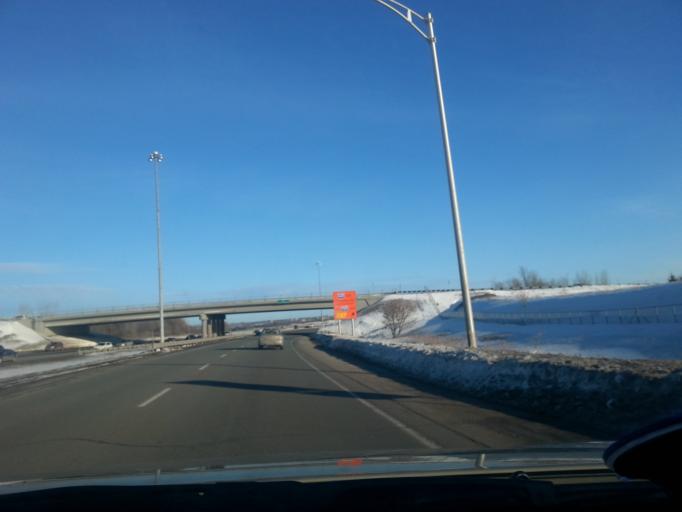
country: CA
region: Quebec
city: L'Ancienne-Lorette
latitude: 46.8171
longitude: -71.3480
